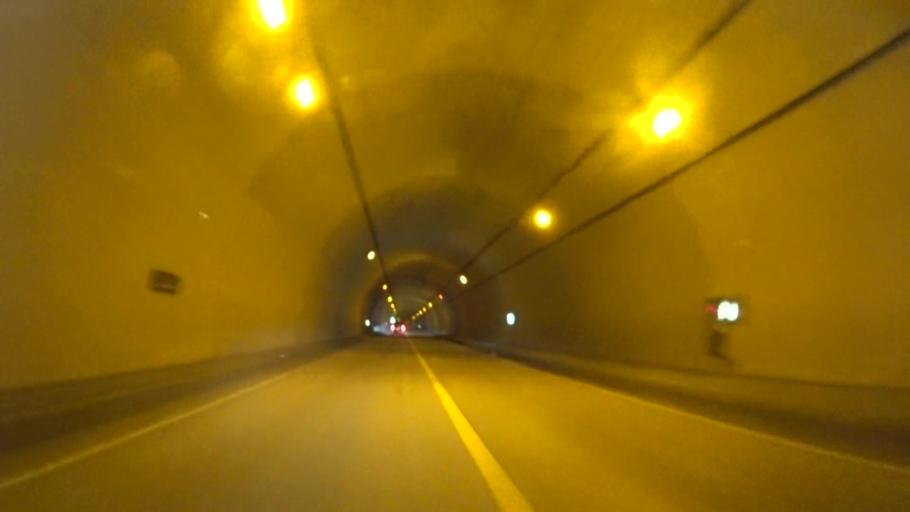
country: JP
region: Kyoto
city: Fukuchiyama
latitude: 35.4014
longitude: 135.0382
